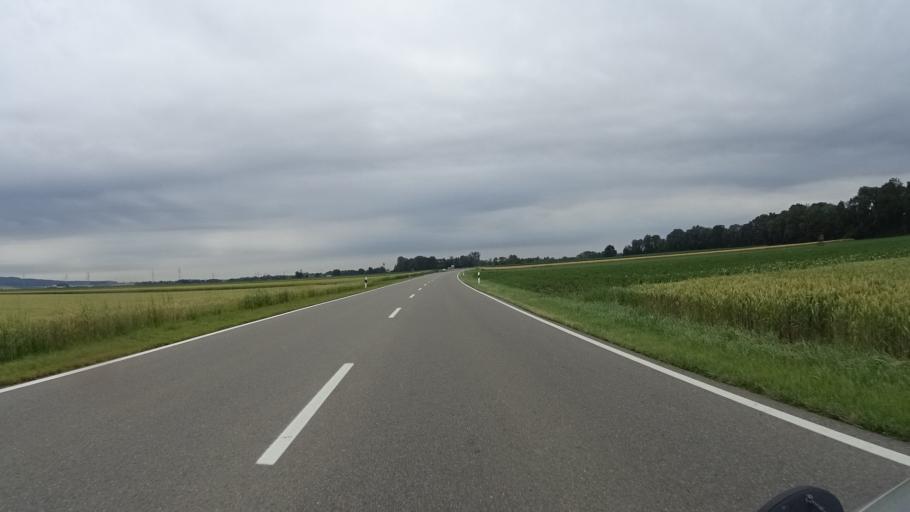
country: DE
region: Bavaria
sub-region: Swabia
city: Fellheim
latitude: 48.0611
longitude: 10.1529
